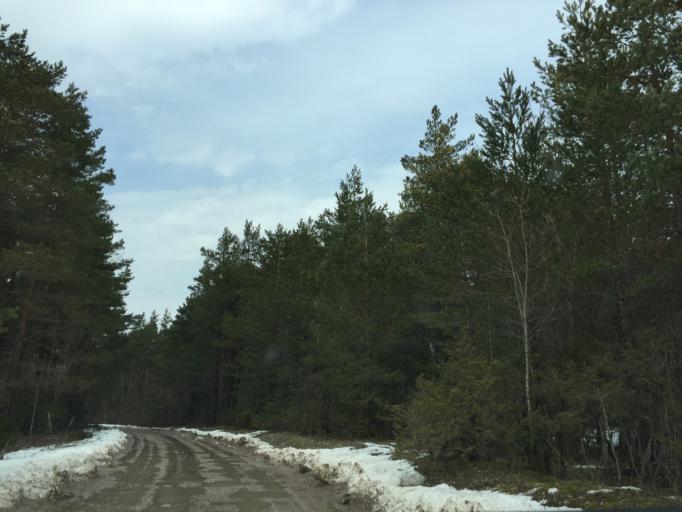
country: EE
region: Saare
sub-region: Kuressaare linn
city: Kuressaare
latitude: 58.4300
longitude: 22.1445
